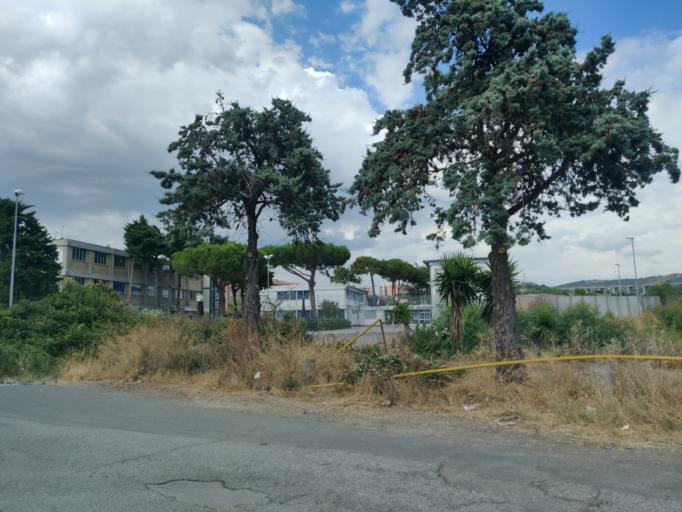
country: IT
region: Latium
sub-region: Citta metropolitana di Roma Capitale
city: Civitavecchia
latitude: 42.0868
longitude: 11.8103
